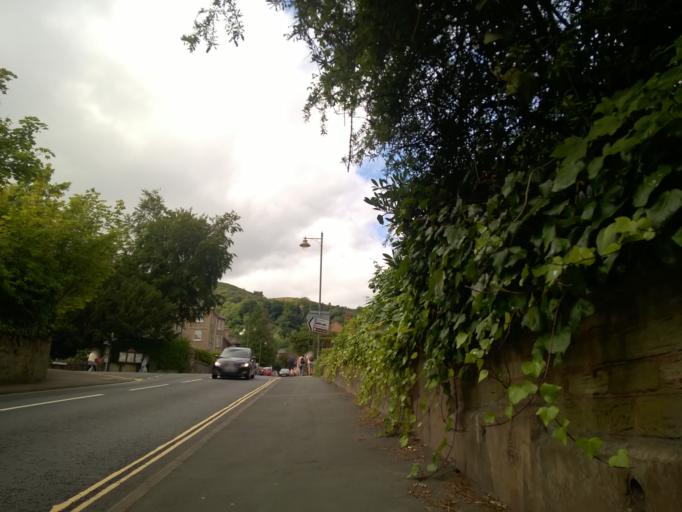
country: GB
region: England
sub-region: Worcestershire
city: Great Malvern
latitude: 52.1118
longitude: -2.3246
